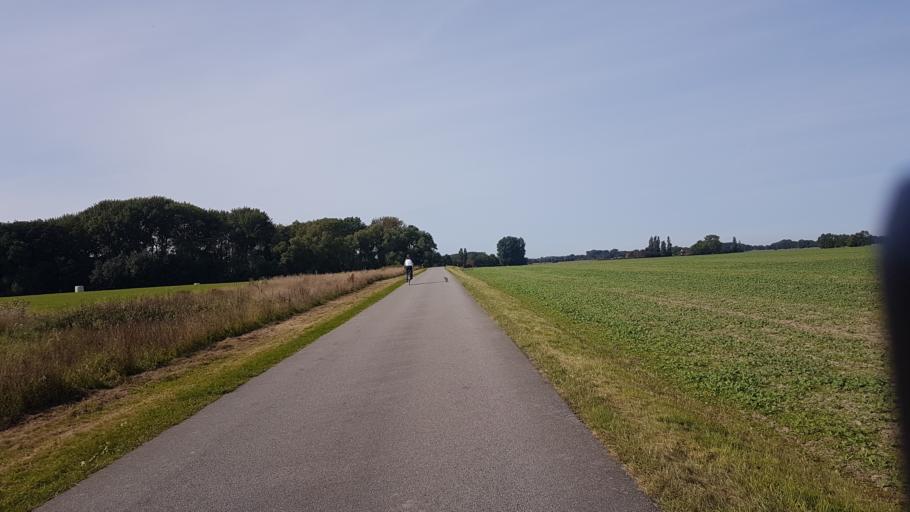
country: DE
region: Mecklenburg-Vorpommern
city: Gingst
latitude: 54.4209
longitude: 13.2345
